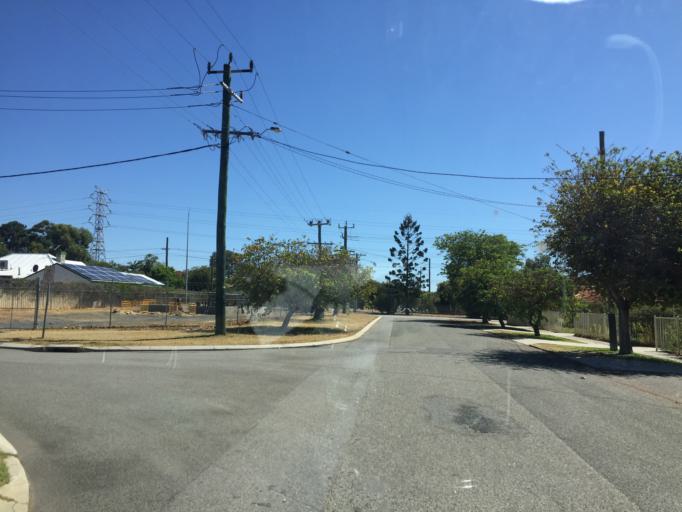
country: AU
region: Western Australia
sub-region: Victoria Park
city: Victoria Park
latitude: -31.9817
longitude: 115.9134
